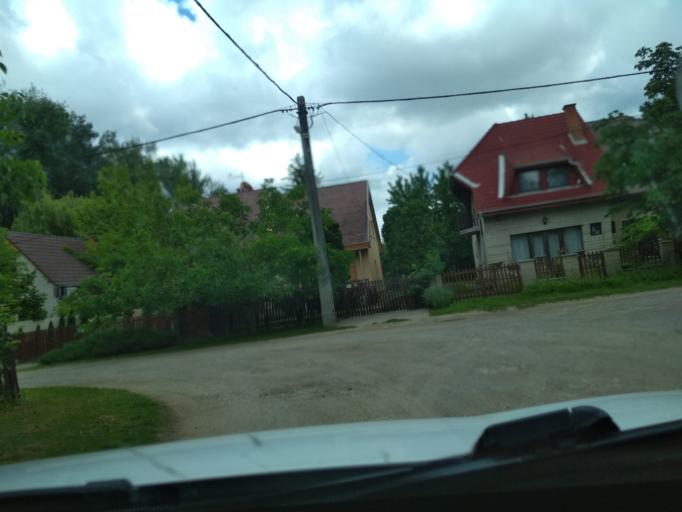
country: HU
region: Jasz-Nagykun-Szolnok
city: Tiszafured
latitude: 47.6190
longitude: 20.7385
